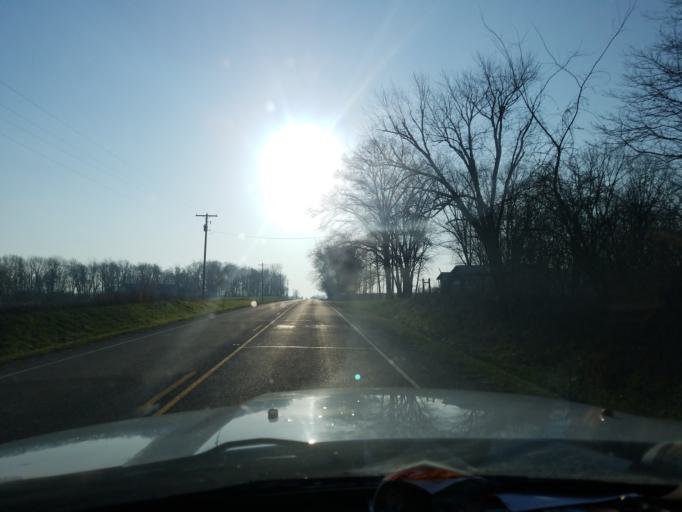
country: US
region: Indiana
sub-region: Vigo County
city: Seelyville
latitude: 39.3898
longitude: -87.2285
